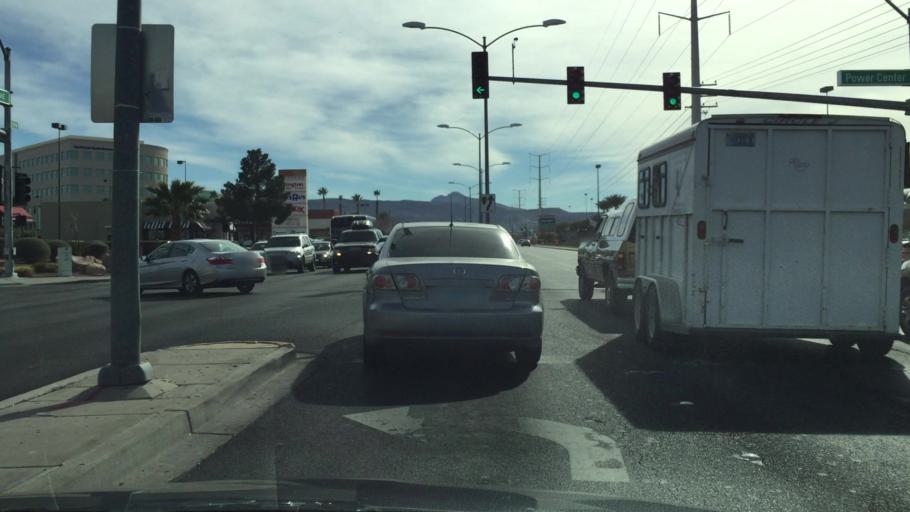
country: US
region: Nevada
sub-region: Clark County
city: Whitney
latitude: 36.0600
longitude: -115.0462
